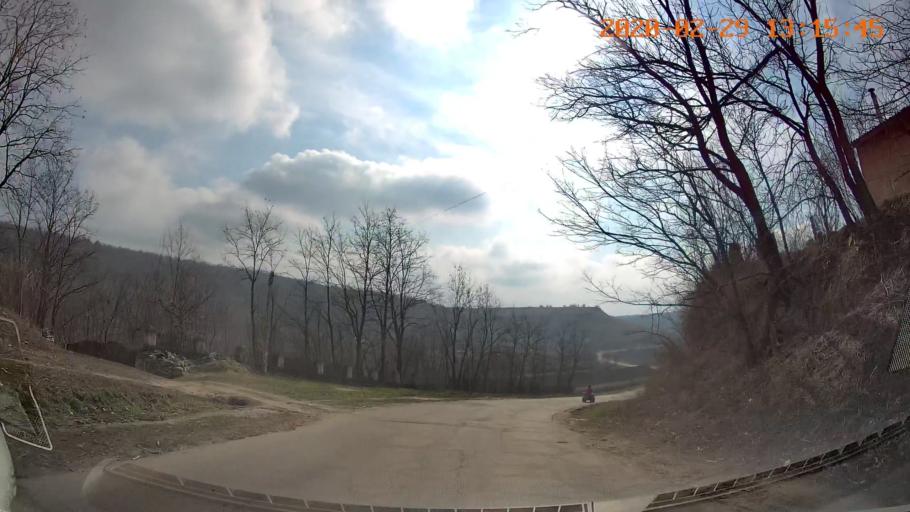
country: MD
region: Telenesti
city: Camenca
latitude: 48.0078
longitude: 28.6682
